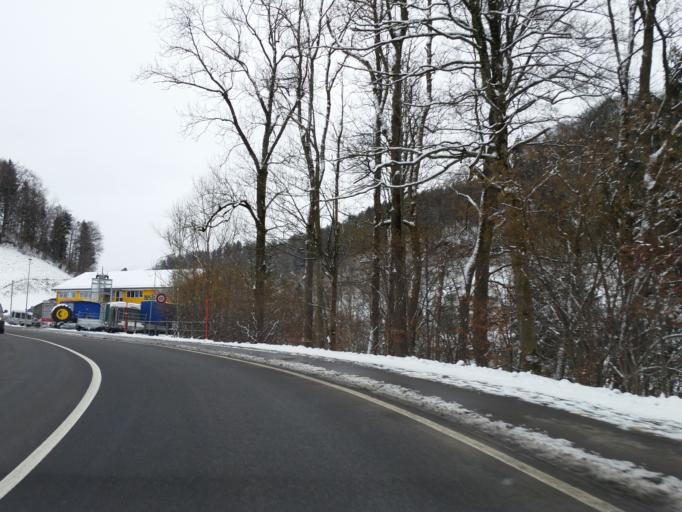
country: CH
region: Appenzell Ausserrhoden
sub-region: Bezirk Mittelland
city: Buhler
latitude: 47.3671
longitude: 9.4310
